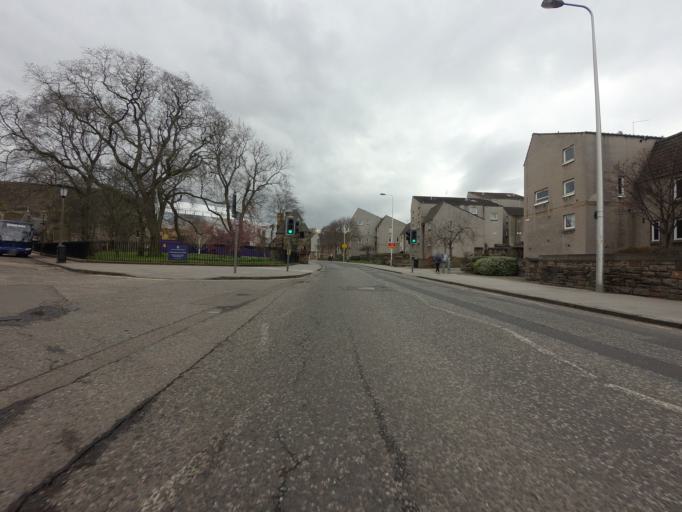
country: GB
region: Scotland
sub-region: Edinburgh
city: Edinburgh
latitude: 55.9538
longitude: -3.1739
